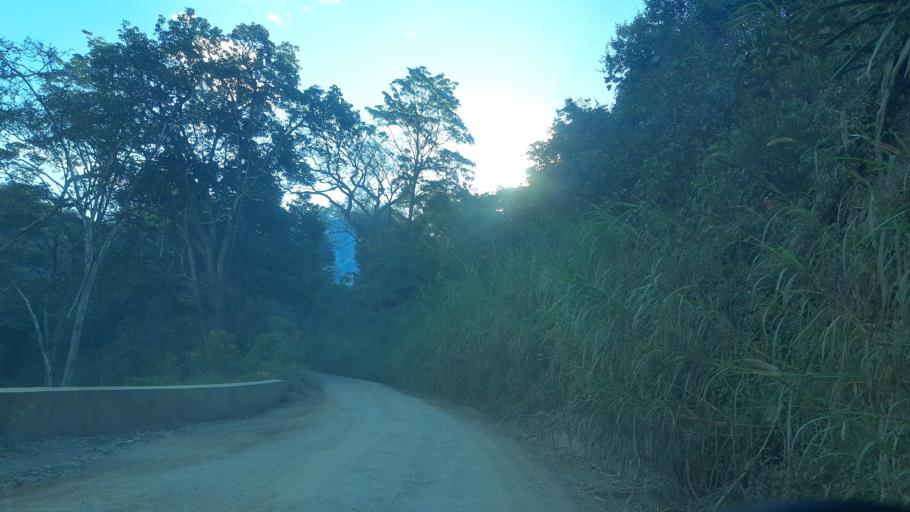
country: CO
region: Boyaca
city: Garagoa
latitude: 5.0825
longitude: -73.3889
